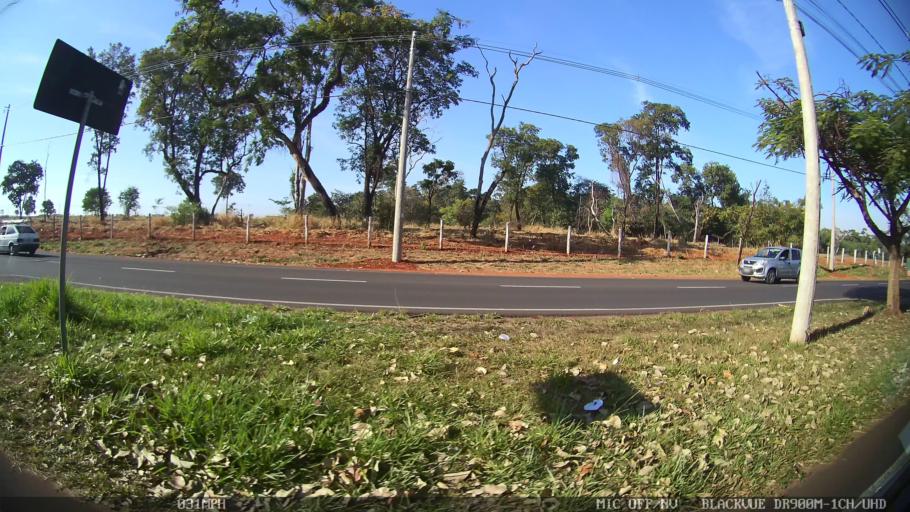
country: BR
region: Sao Paulo
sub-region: Sao Jose Do Rio Preto
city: Sao Jose do Rio Preto
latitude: -20.7648
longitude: -49.3517
